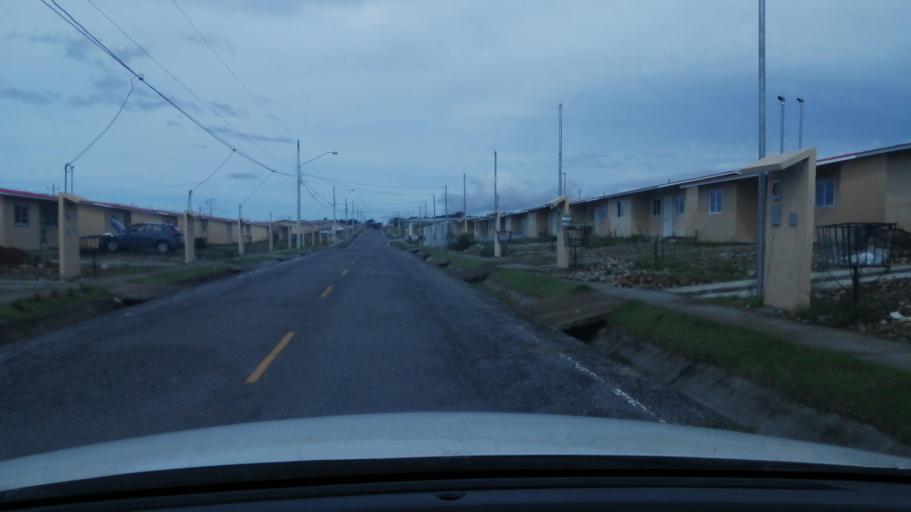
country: PA
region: Chiriqui
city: Potrerillos Abajo
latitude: 8.6665
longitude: -82.4289
